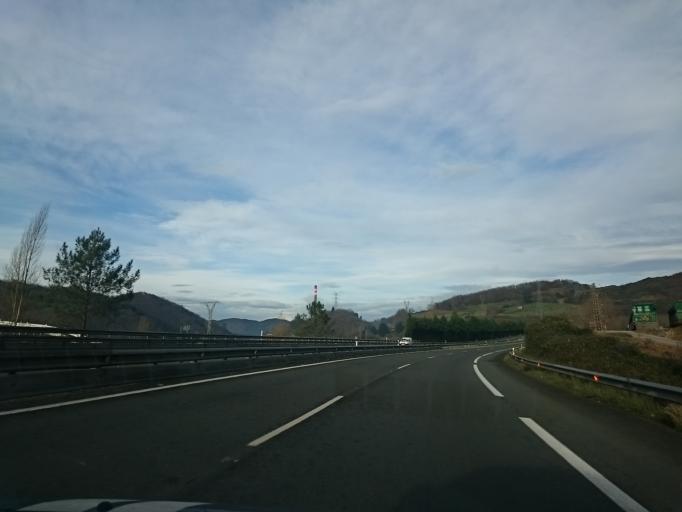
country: ES
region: Asturias
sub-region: Province of Asturias
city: Castandiello
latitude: 43.3085
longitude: -5.8596
